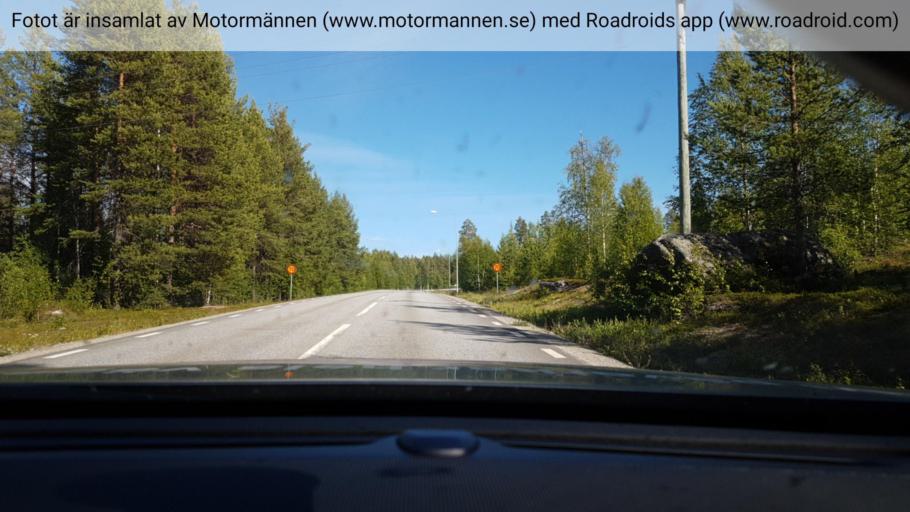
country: SE
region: Vaesterbotten
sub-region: Lycksele Kommun
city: Lycksele
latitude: 64.6386
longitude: 18.5264
